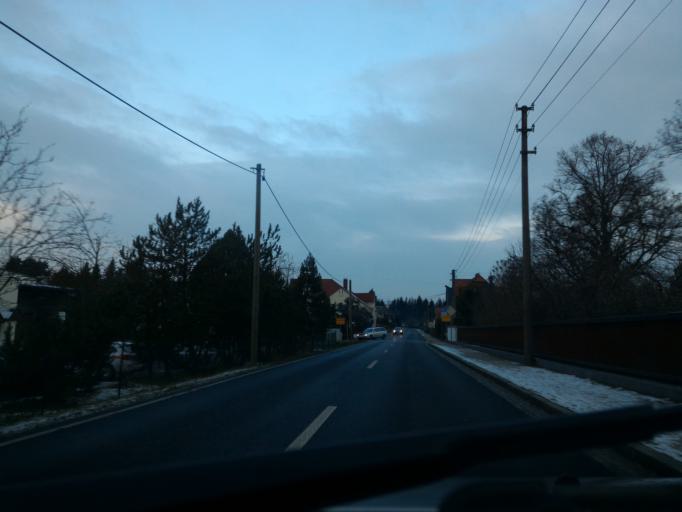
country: DE
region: Saxony
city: Leutersdorf
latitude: 50.9509
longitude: 14.6632
